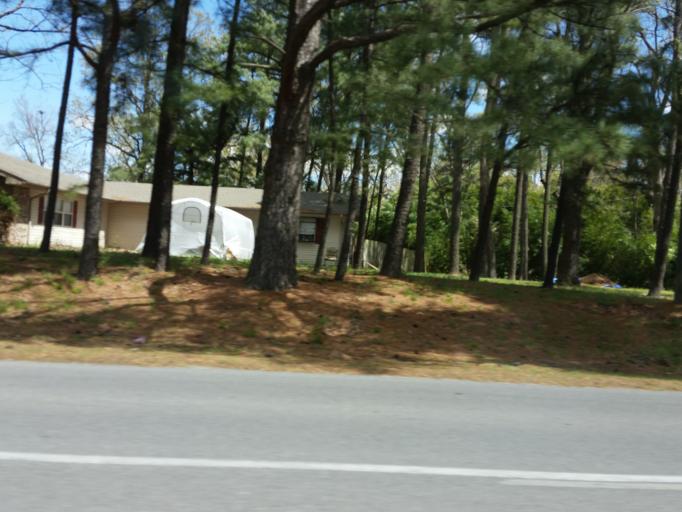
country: US
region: Arkansas
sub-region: Craighead County
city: Jonesboro
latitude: 35.8136
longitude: -90.7008
